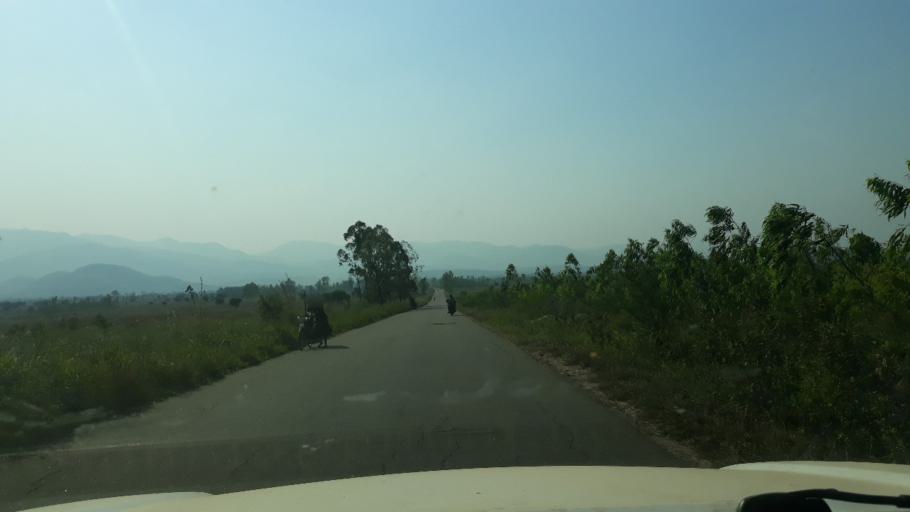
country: BI
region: Cibitoke
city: Cibitoke
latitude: -2.8349
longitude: 29.0159
